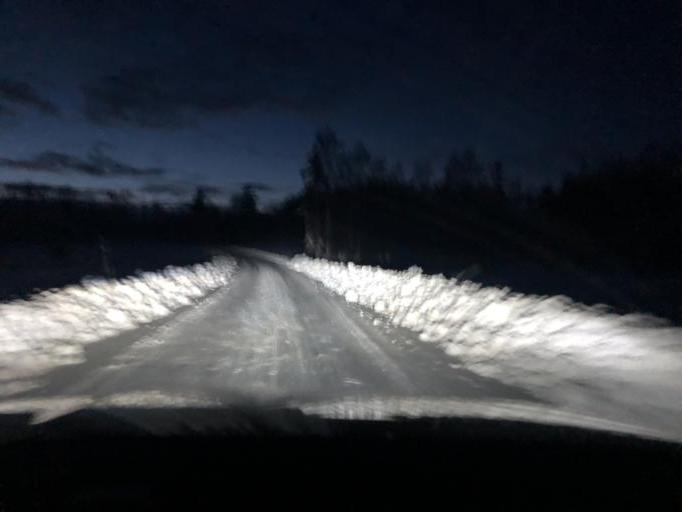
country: SE
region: Vaesternorrland
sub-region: Kramfors Kommun
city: Bollstabruk
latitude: 63.0553
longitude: 17.6655
